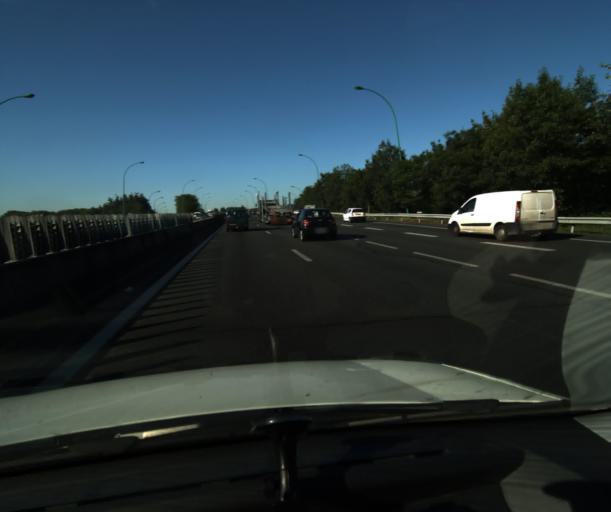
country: FR
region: Midi-Pyrenees
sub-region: Departement de la Haute-Garonne
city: Balma
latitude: 43.5755
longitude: 1.4968
